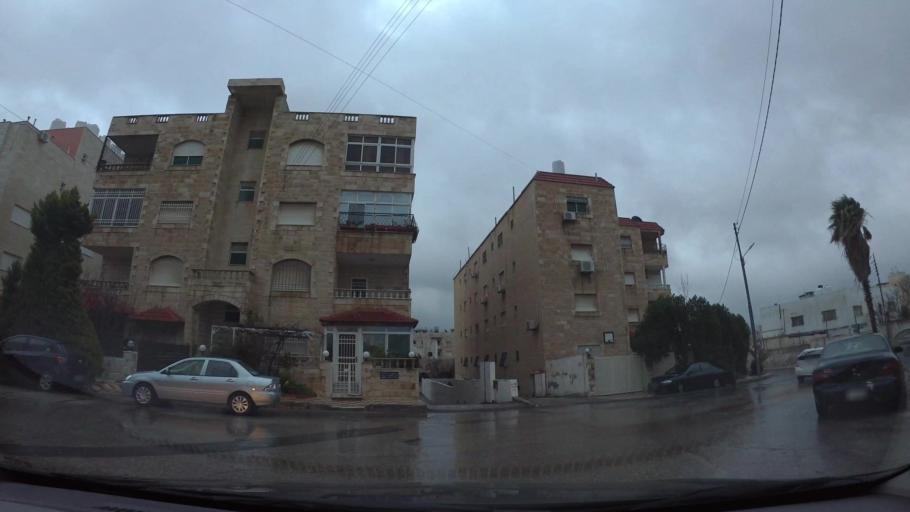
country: JO
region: Amman
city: Amman
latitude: 31.9966
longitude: 35.9287
